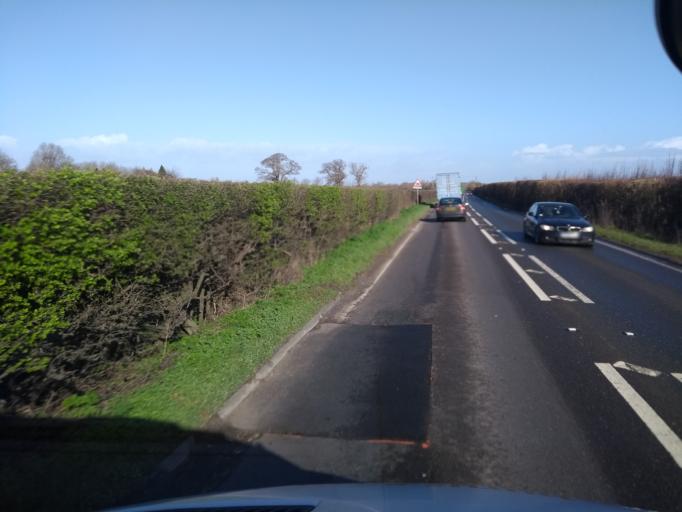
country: GB
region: England
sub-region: Somerset
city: Ilchester
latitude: 50.9902
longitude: -2.6782
